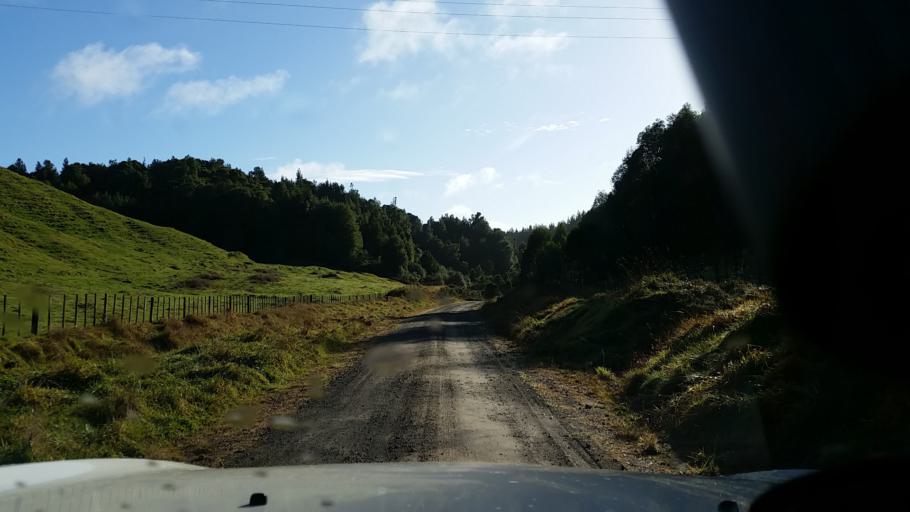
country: NZ
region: Bay of Plenty
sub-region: Kawerau District
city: Kawerau
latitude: -38.0116
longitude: 176.5973
